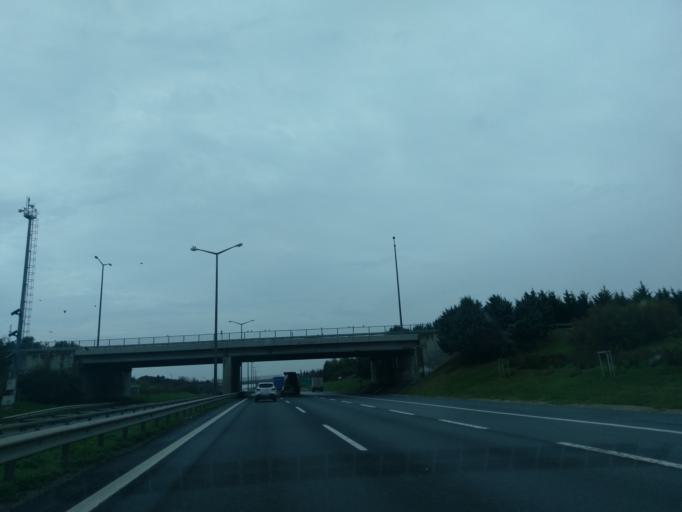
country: TR
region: Istanbul
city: Silivri
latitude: 41.1112
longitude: 28.2653
